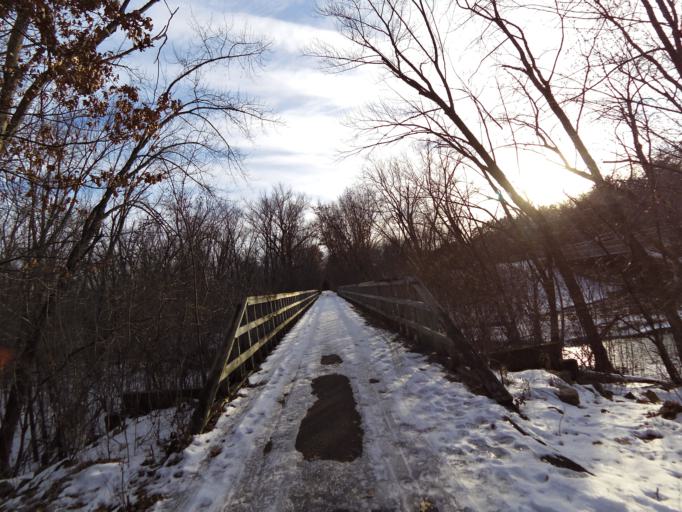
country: US
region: Minnesota
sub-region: Washington County
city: Afton
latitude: 44.9113
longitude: -92.7795
